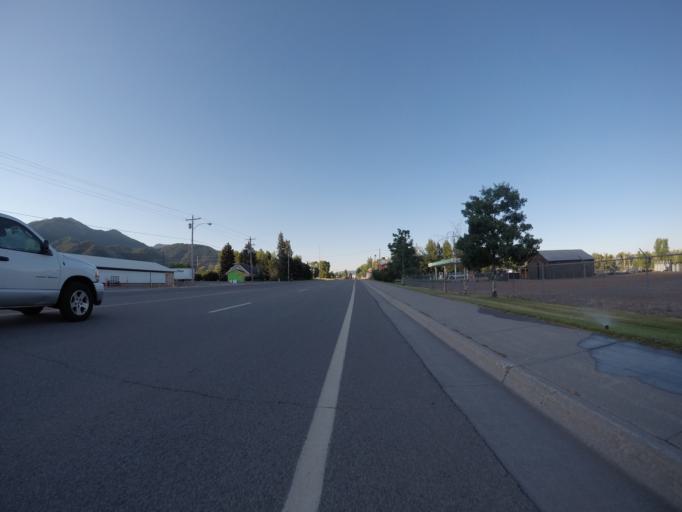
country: US
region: Wyoming
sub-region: Lincoln County
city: Afton
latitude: 42.7348
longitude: -110.9334
